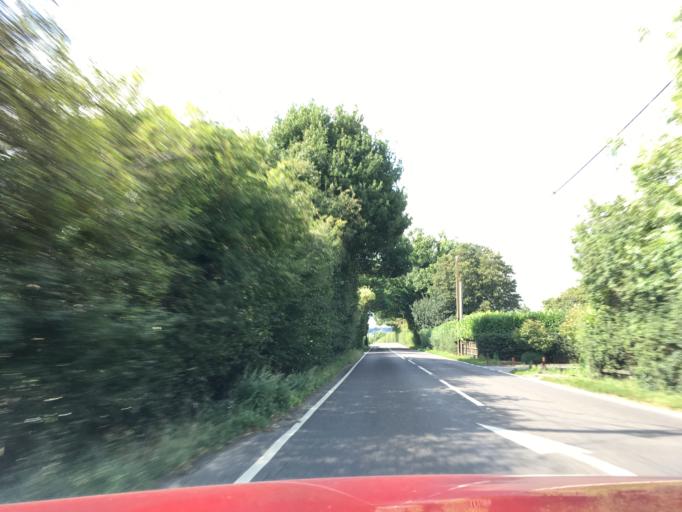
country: GB
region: England
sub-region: Kent
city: Headcorn
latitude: 51.1943
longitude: 0.6003
